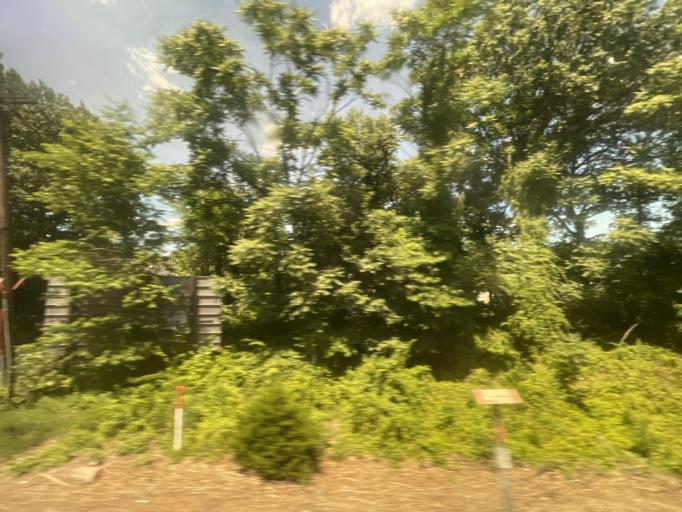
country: US
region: New Jersey
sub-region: Middlesex County
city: Metuchen
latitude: 40.5558
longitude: -74.3435
